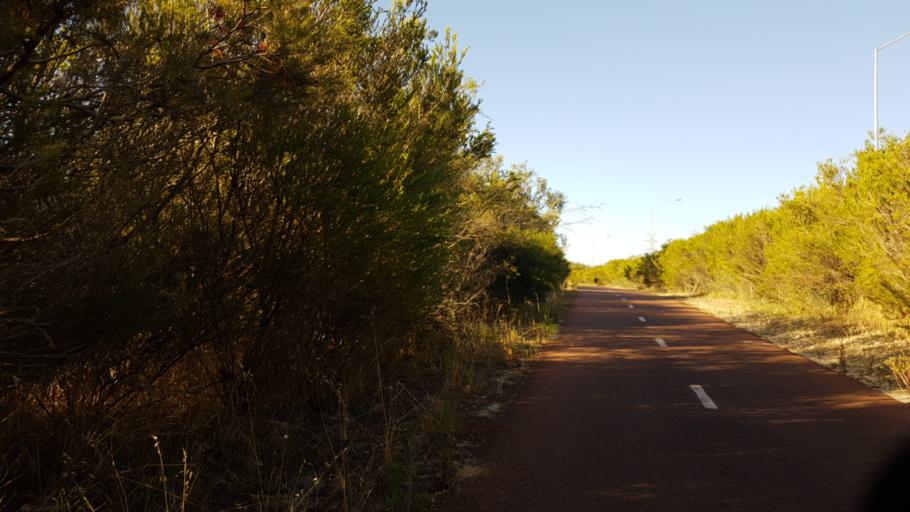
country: AU
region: Western Australia
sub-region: Kwinana
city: Wellard
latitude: -32.2624
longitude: 115.8521
